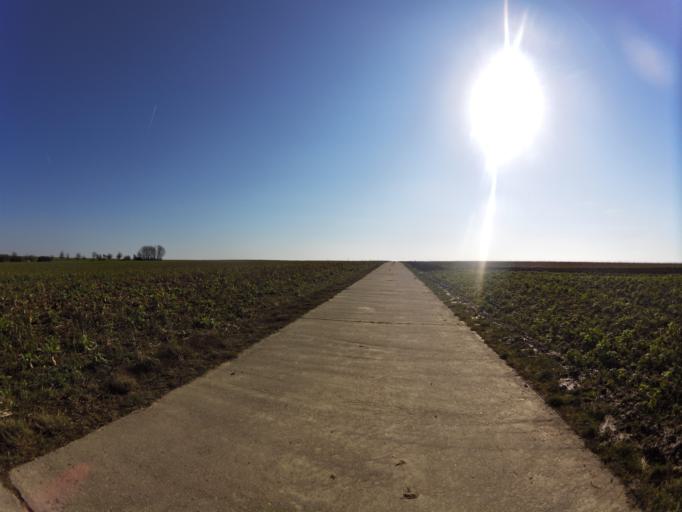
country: DE
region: Bavaria
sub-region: Regierungsbezirk Unterfranken
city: Eibelstadt
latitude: 49.6929
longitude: 9.9733
